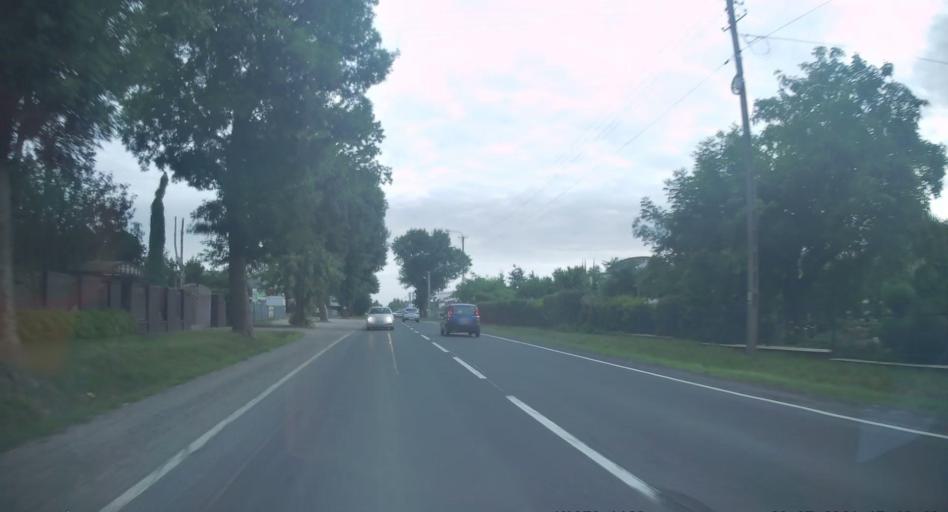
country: PL
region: Lodz Voivodeship
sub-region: Powiat radomszczanski
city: Radomsko
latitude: 51.1022
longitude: 19.4629
